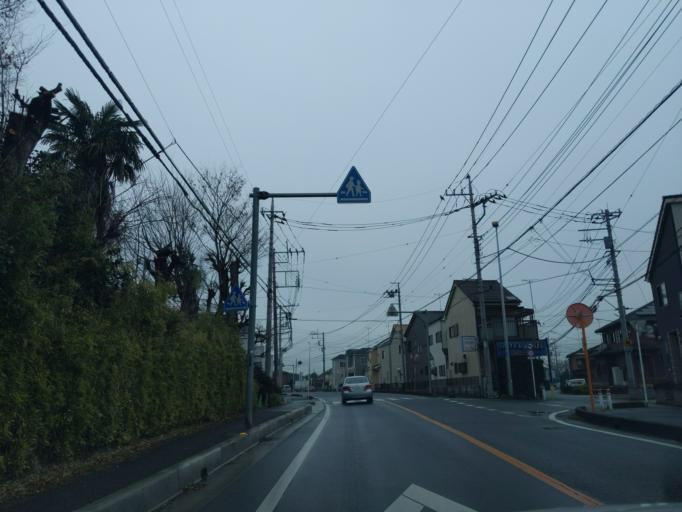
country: JP
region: Saitama
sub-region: Kawaguchi-shi
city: Hatogaya-honcho
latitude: 35.8607
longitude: 139.7316
